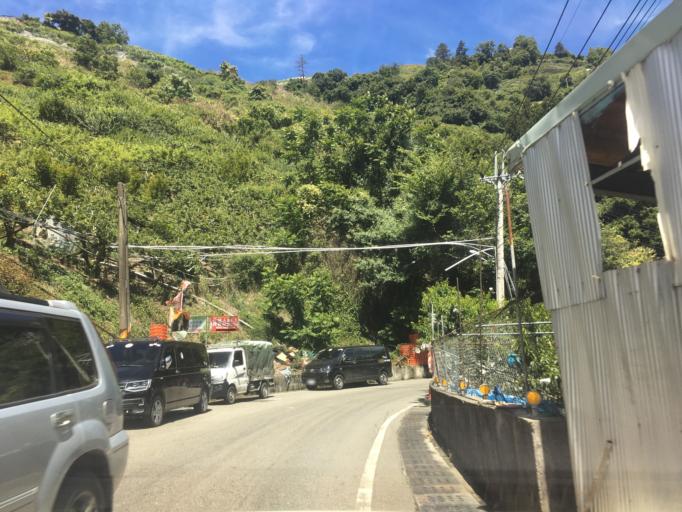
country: TW
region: Taiwan
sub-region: Nantou
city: Puli
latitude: 24.2452
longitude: 121.2547
